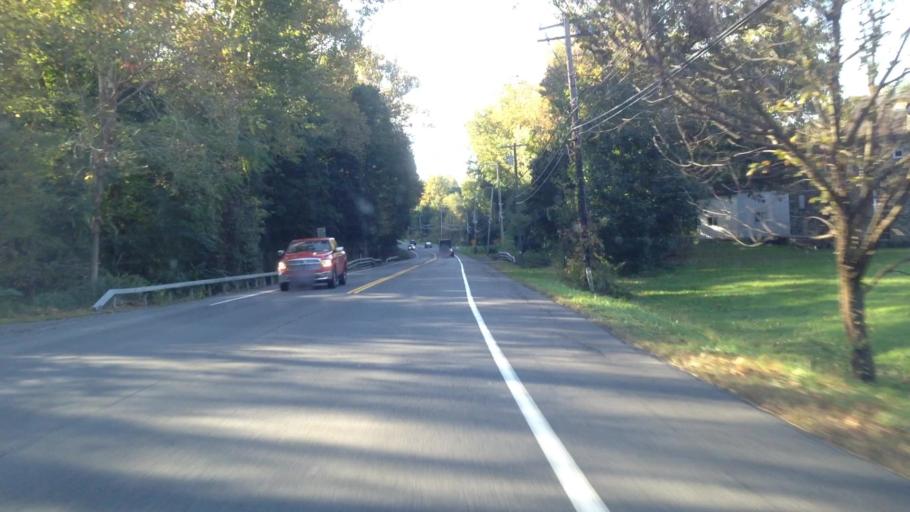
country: US
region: New York
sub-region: Dutchess County
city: Hyde Park
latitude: 41.8193
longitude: -73.9642
